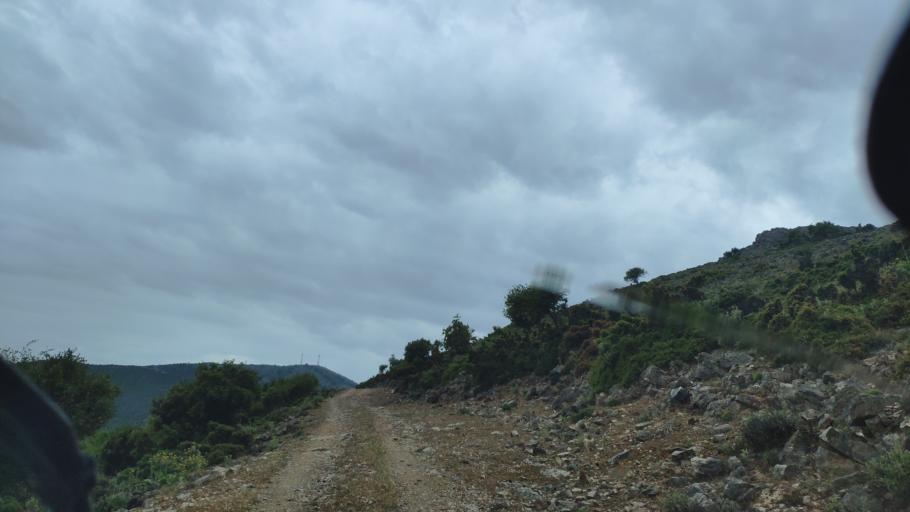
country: GR
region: West Greece
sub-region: Nomos Aitolias kai Akarnanias
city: Archontochorion
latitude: 38.6744
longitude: 21.0147
